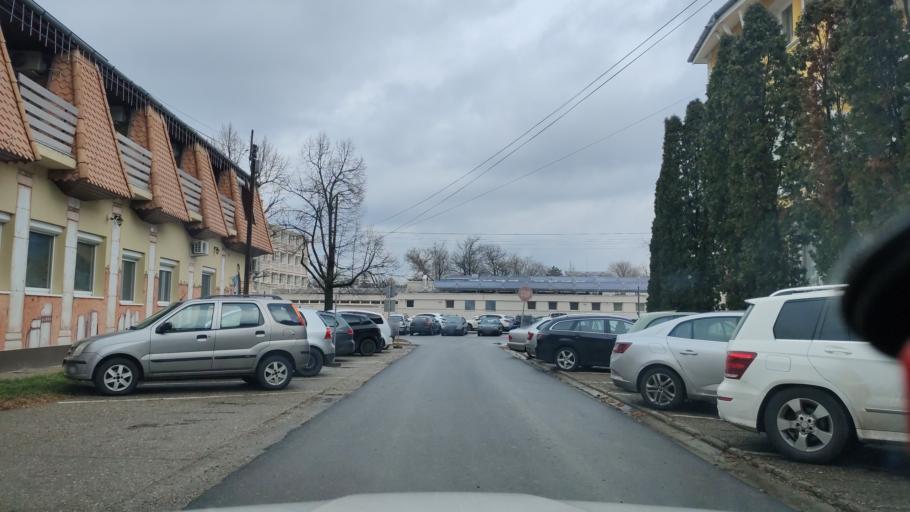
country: HU
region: Hajdu-Bihar
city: Hajduszoboszlo
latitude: 47.4498
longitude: 21.3972
